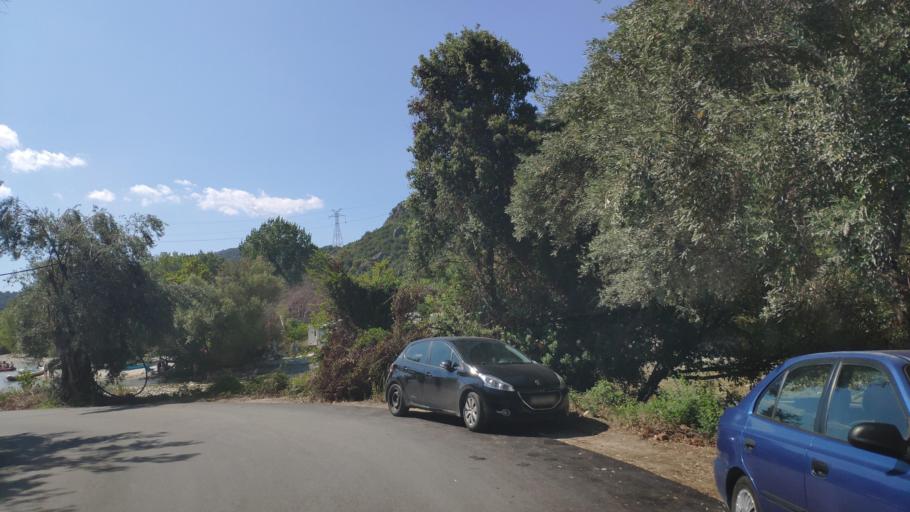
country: GR
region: Epirus
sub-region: Nomos Prevezis
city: Kanalaki
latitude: 39.3268
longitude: 20.6189
